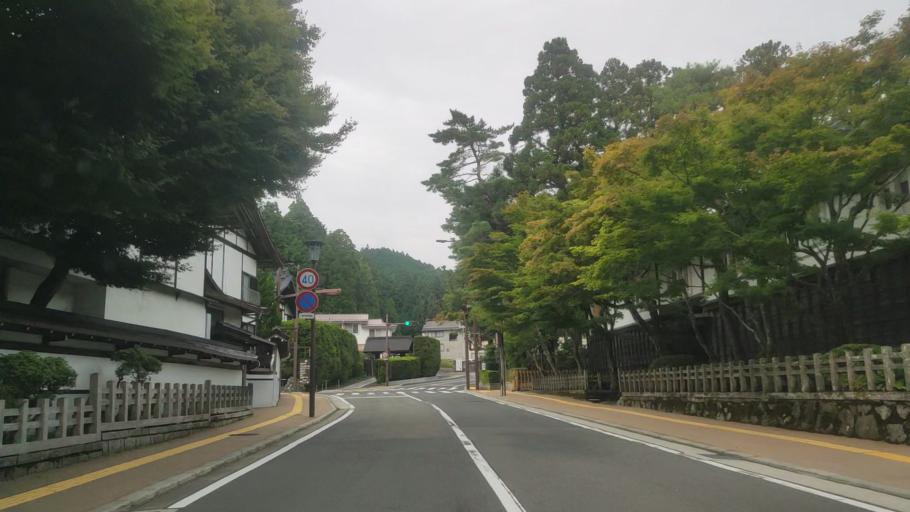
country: JP
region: Wakayama
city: Koya
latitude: 34.2149
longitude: 135.5862
